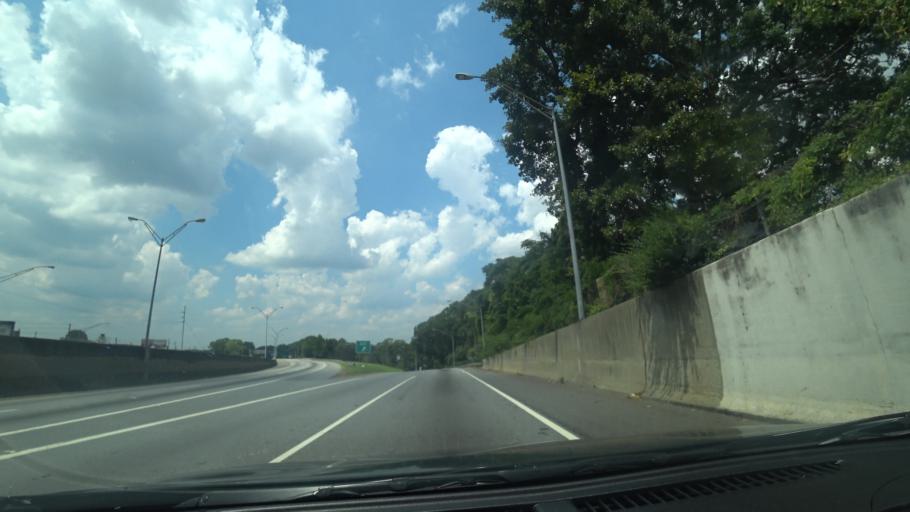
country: US
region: Georgia
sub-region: Fulton County
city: East Point
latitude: 33.6977
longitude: -84.4162
